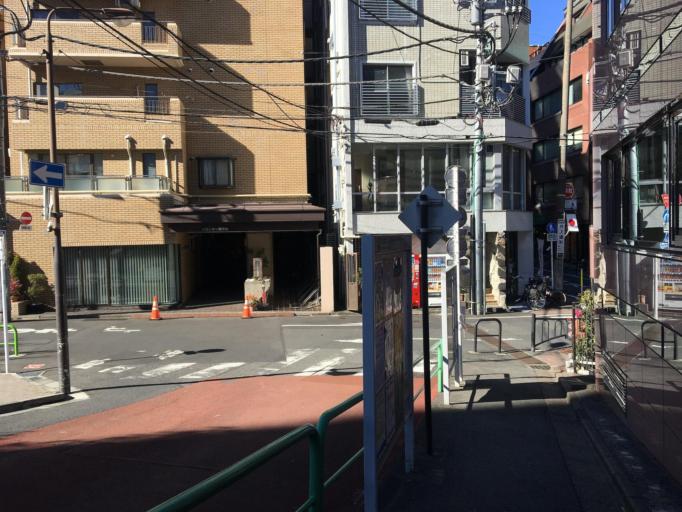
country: JP
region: Tokyo
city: Tokyo
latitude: 35.6993
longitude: 139.7473
